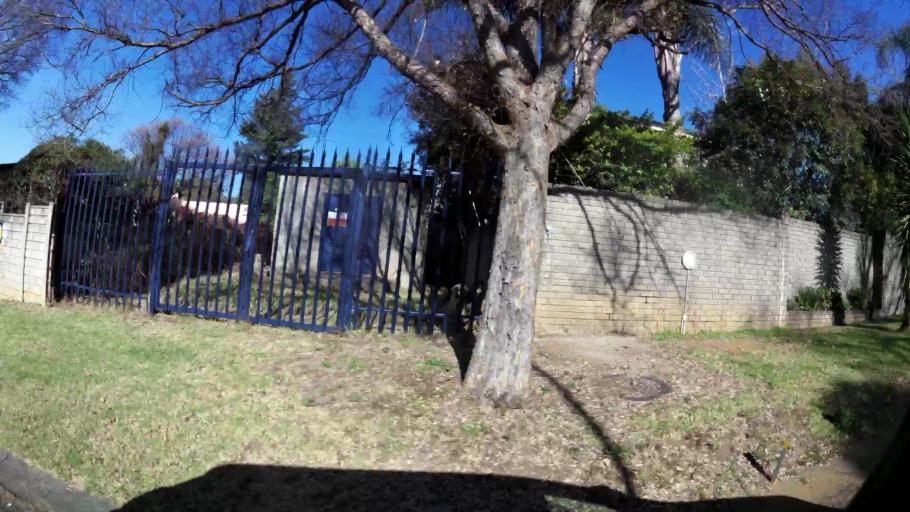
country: ZA
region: Gauteng
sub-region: City of Johannesburg Metropolitan Municipality
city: Johannesburg
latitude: -26.0963
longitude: 27.9786
